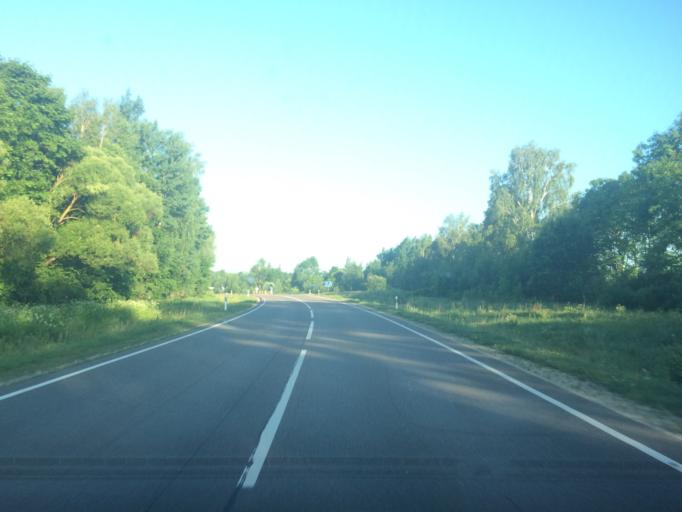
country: LT
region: Utenos apskritis
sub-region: Anyksciai
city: Anyksciai
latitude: 55.4058
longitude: 25.1134
